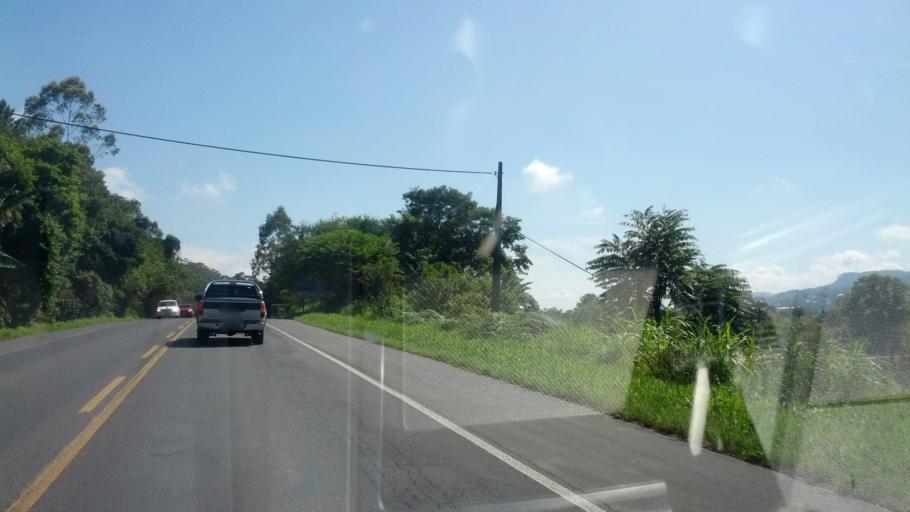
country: BR
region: Santa Catarina
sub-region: Rio Do Sul
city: Rio do Sul
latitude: -27.2265
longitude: -49.6665
